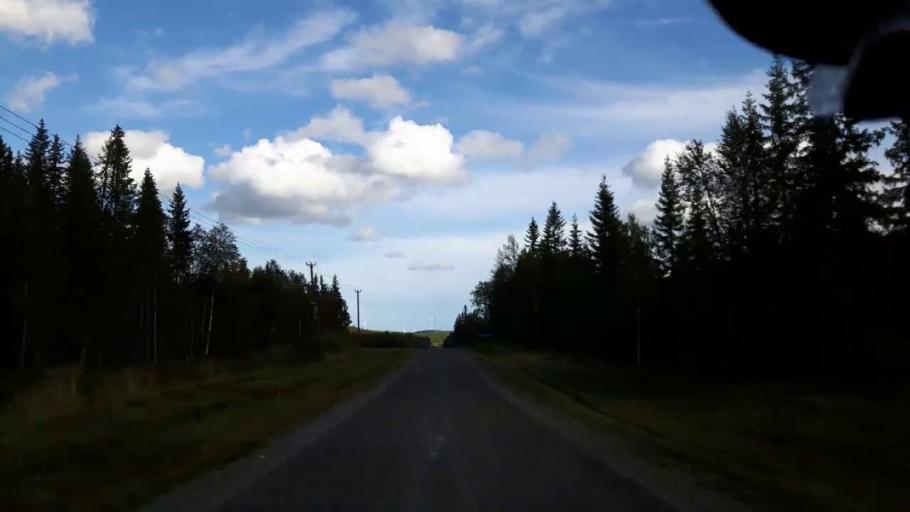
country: SE
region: Jaemtland
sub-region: Ragunda Kommun
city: Hammarstrand
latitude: 63.4388
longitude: 15.9974
